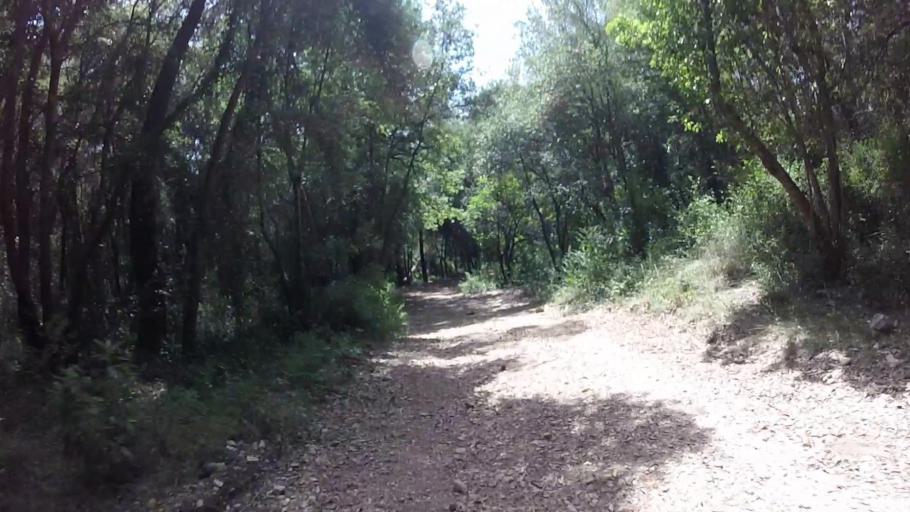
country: FR
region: Provence-Alpes-Cote d'Azur
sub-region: Departement des Alpes-Maritimes
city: Mougins
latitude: 43.6144
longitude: 7.0258
